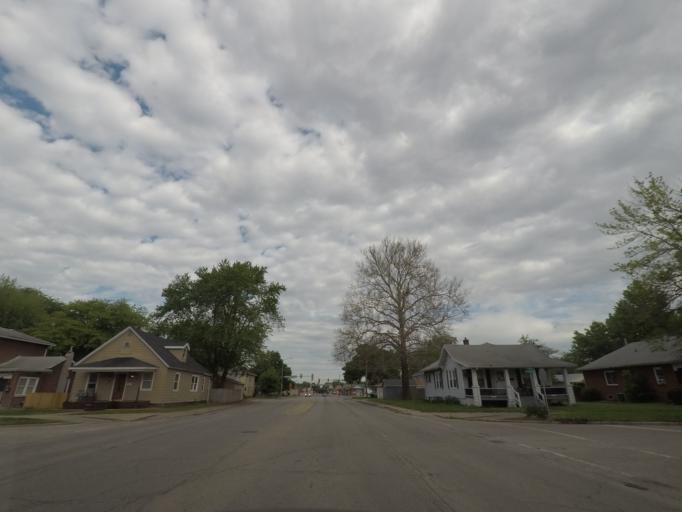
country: US
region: Illinois
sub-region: Logan County
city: Lincoln
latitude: 40.1507
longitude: -89.3559
